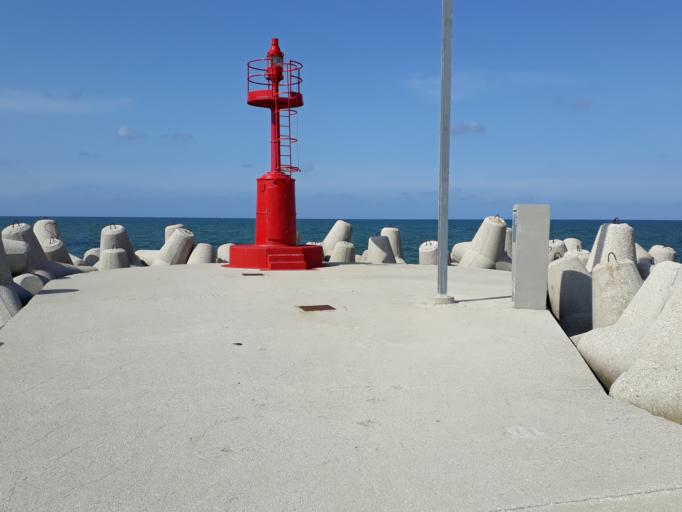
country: IT
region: The Marches
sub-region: Provincia di Pesaro e Urbino
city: Fano
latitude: 43.8560
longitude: 13.0166
